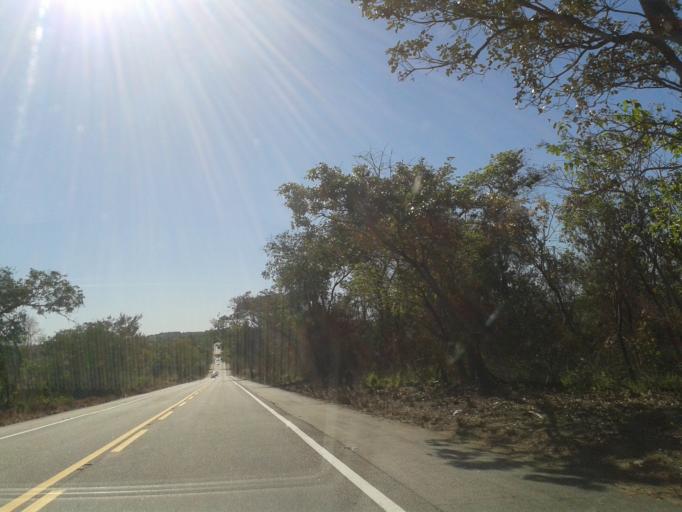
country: BR
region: Goias
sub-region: Goias
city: Goias
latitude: -15.7609
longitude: -50.1590
